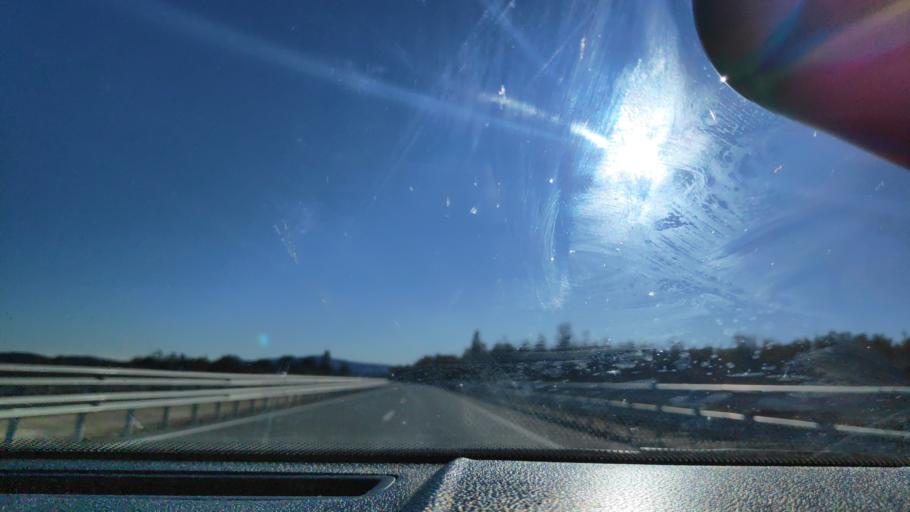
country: ES
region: Extremadura
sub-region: Provincia de Badajoz
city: Monesterio
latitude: 38.0098
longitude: -6.2298
